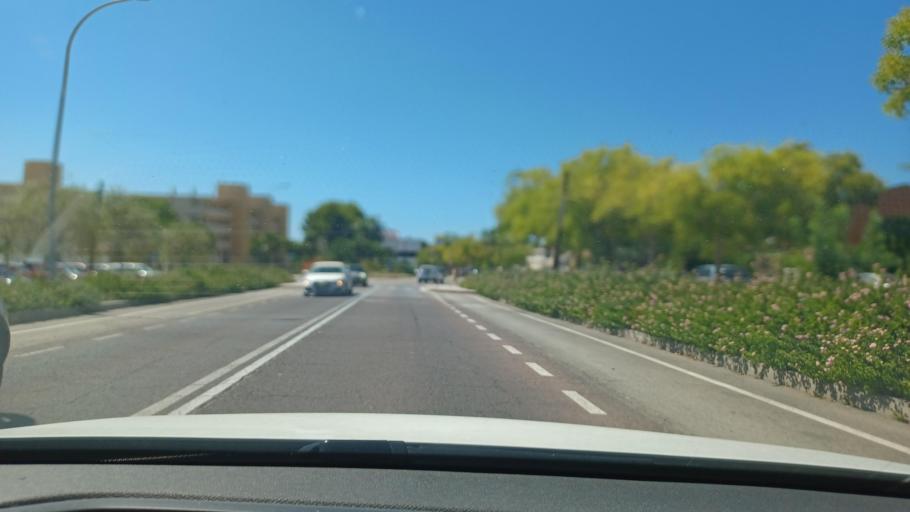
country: ES
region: Catalonia
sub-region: Provincia de Tarragona
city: Sant Carles de la Rapita
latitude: 40.6087
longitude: 0.5837
